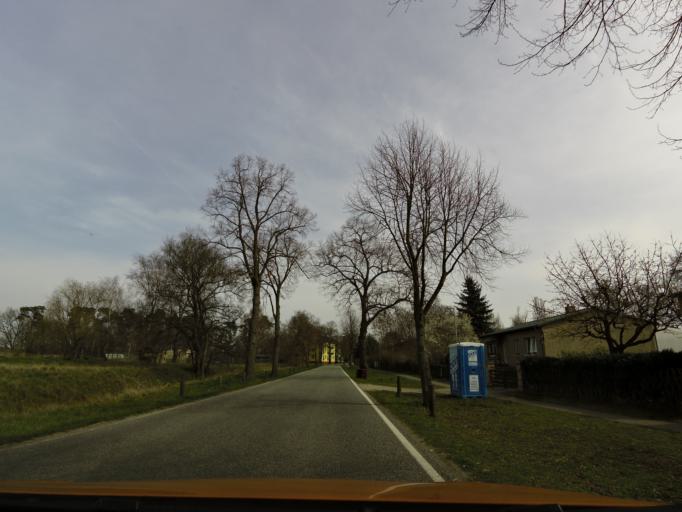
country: DE
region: Brandenburg
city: Stahnsdorf
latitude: 52.3398
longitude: 13.2139
